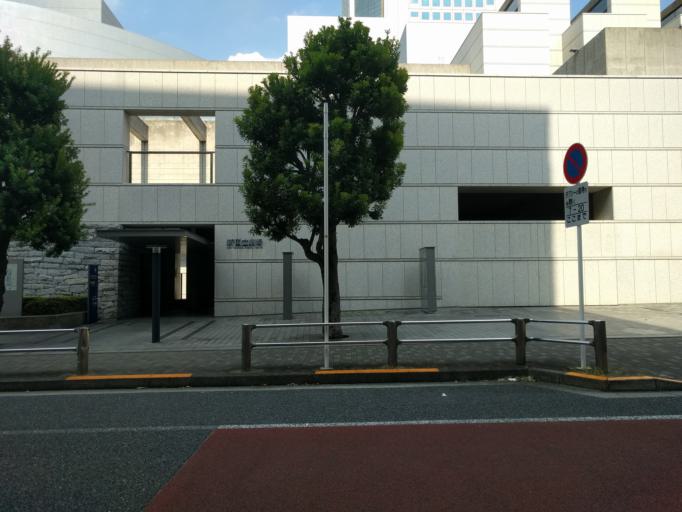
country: JP
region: Tokyo
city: Tokyo
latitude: 35.6822
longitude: 139.6852
